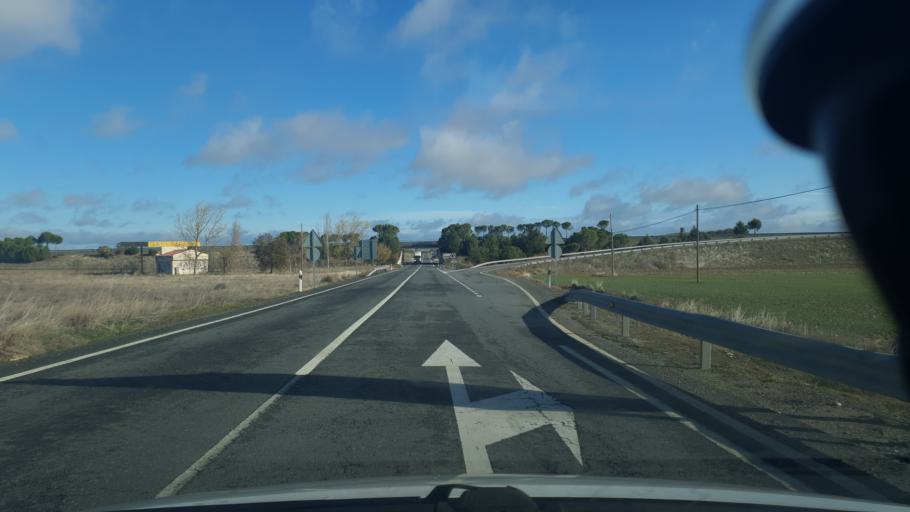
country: ES
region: Castille and Leon
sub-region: Provincia de Segovia
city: Codorniz
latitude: 41.0493
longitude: -4.6266
